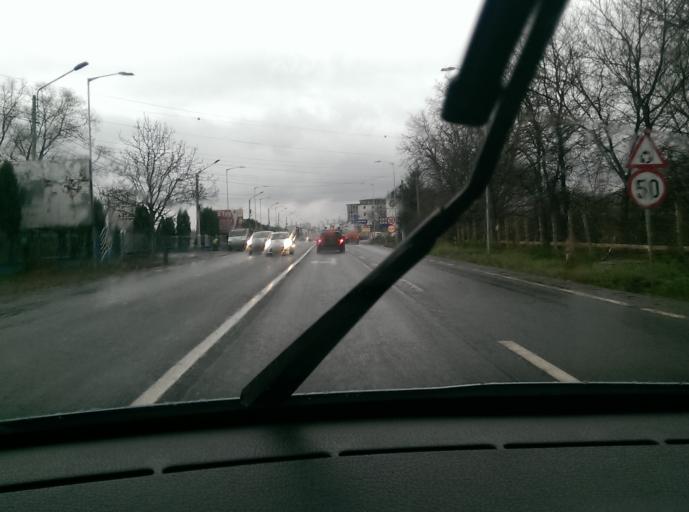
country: RO
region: Cluj
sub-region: Comuna Floresti
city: Floresti
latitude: 46.7501
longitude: 23.5157
